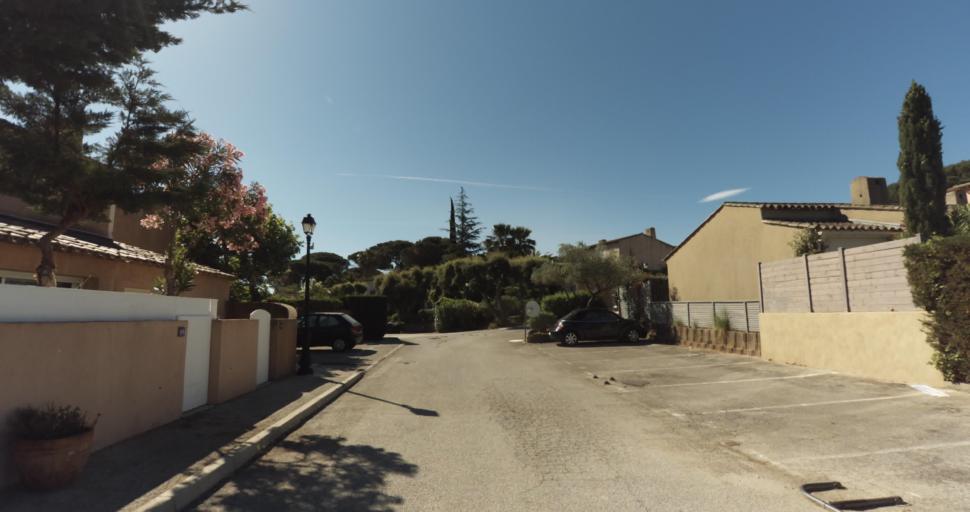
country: FR
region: Provence-Alpes-Cote d'Azur
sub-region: Departement du Var
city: Saint-Tropez
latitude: 43.2609
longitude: 6.6180
